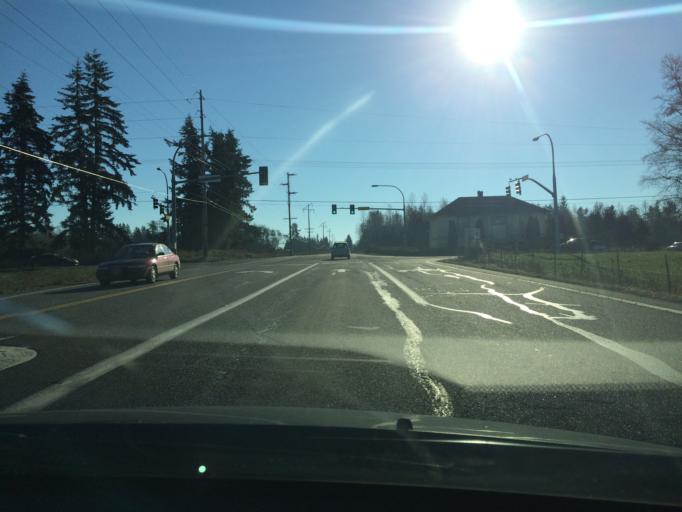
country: US
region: Washington
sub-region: Whatcom County
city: Bellingham
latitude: 48.8340
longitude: -122.4431
